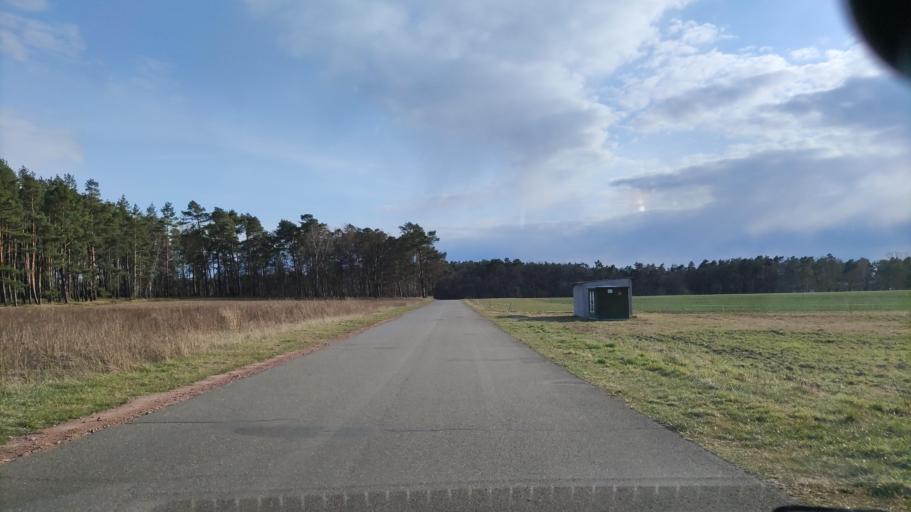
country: DE
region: Lower Saxony
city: Klein Gusborn
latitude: 53.0859
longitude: 11.2223
